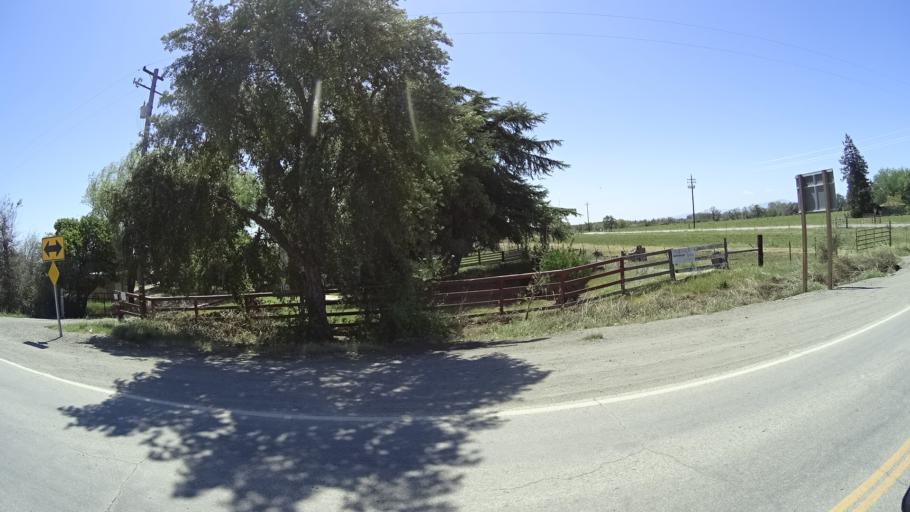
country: US
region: California
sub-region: Glenn County
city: Orland
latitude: 39.7838
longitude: -122.2062
